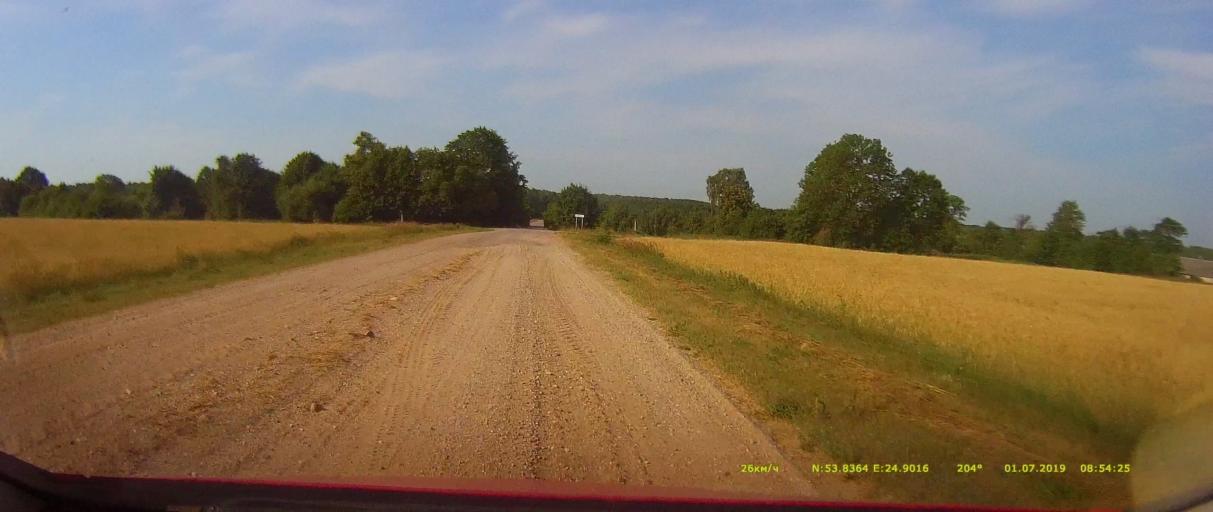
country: BY
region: Grodnenskaya
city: Shchuchin
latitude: 53.8366
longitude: 24.9017
